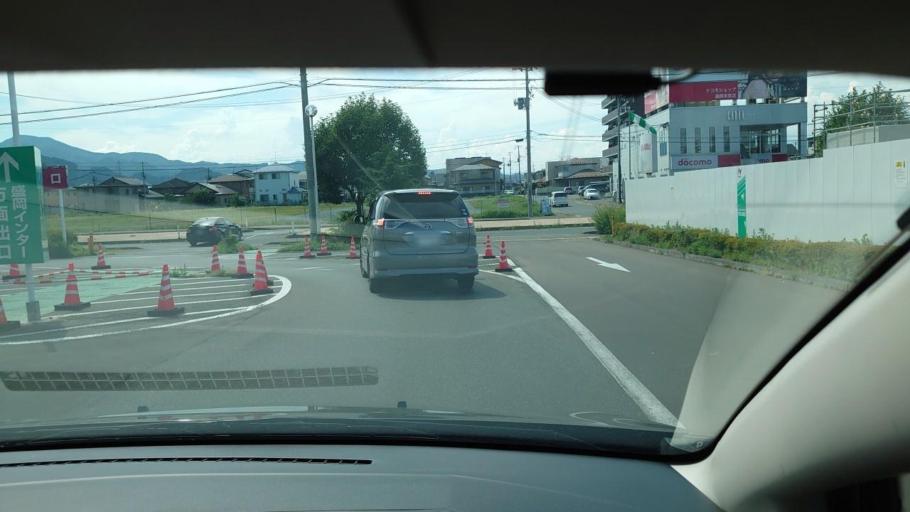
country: JP
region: Iwate
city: Morioka-shi
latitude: 39.6837
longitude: 141.1269
